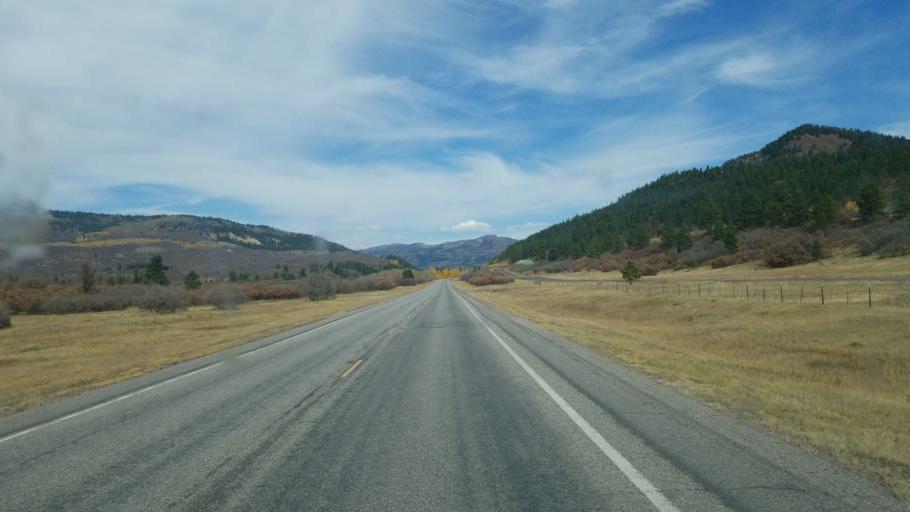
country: US
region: New Mexico
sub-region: Rio Arriba County
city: Chama
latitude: 36.9219
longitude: -106.5610
